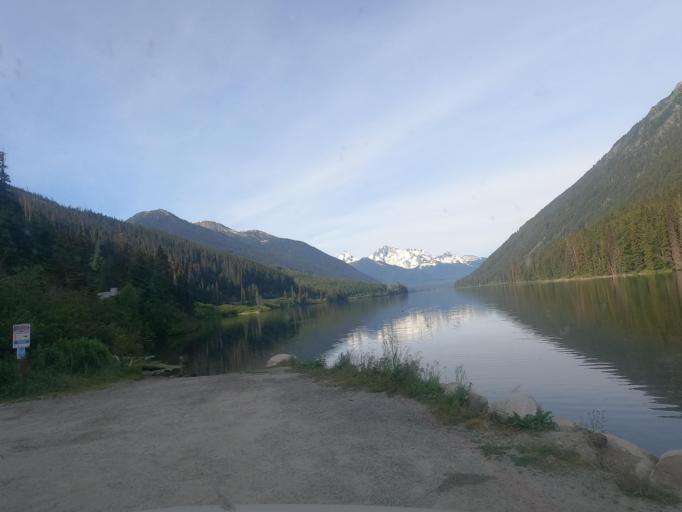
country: CA
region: British Columbia
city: Lillooet
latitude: 50.4189
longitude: -122.2788
